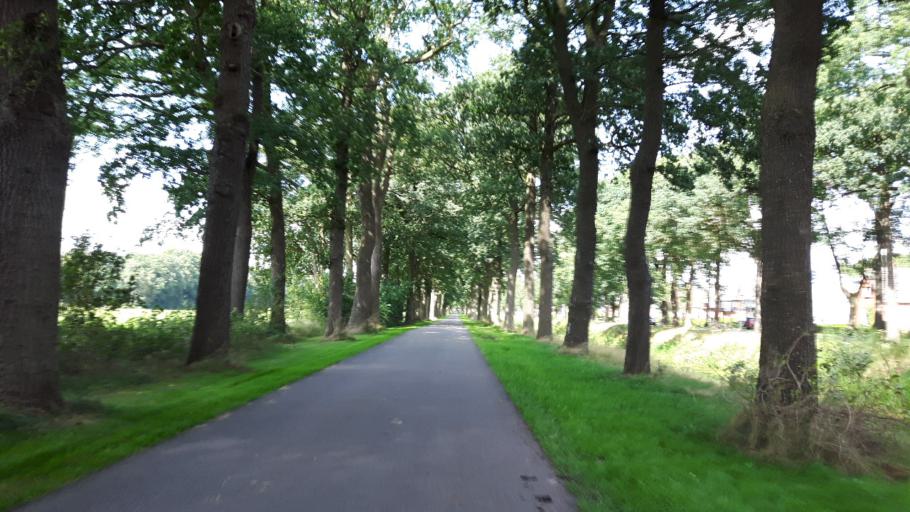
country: NL
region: Friesland
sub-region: Gemeente Smallingerland
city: Drachtstercompagnie
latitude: 53.0758
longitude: 6.2621
